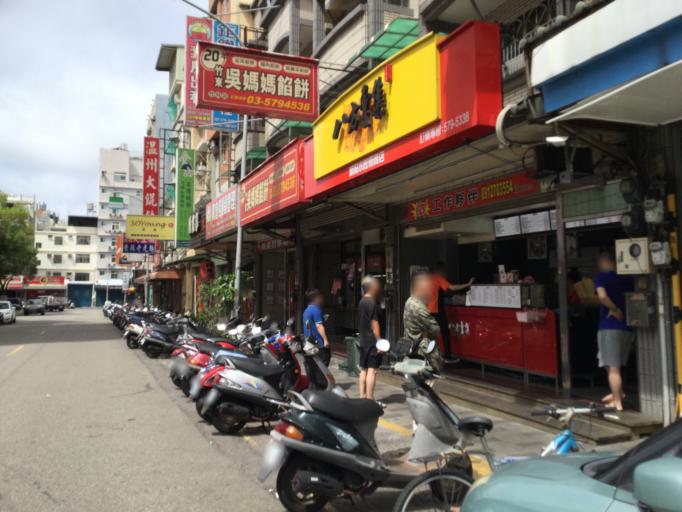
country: TW
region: Taiwan
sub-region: Hsinchu
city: Hsinchu
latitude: 24.7774
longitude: 121.0228
